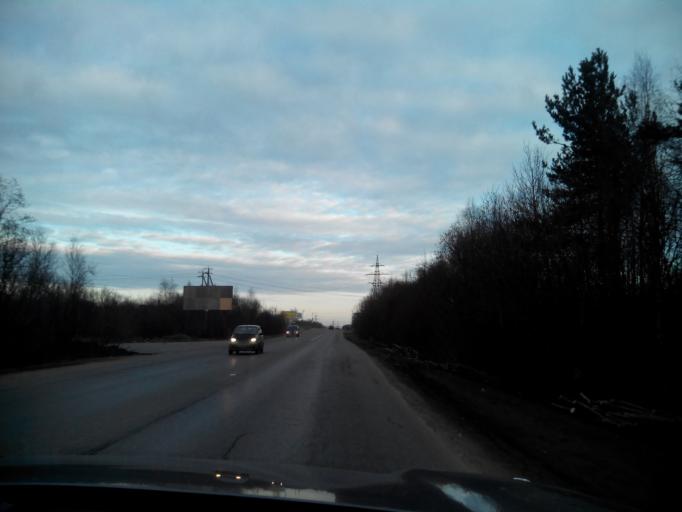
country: RU
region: Arkhangelskaya
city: Arkhangel'sk
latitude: 64.5213
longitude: 40.6722
